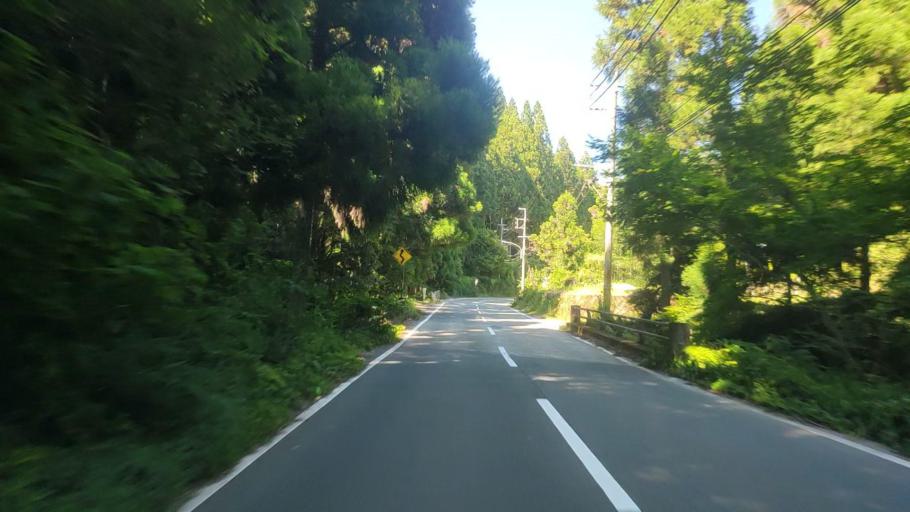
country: JP
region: Nara
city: Yoshino-cho
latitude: 34.4173
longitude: 135.9358
